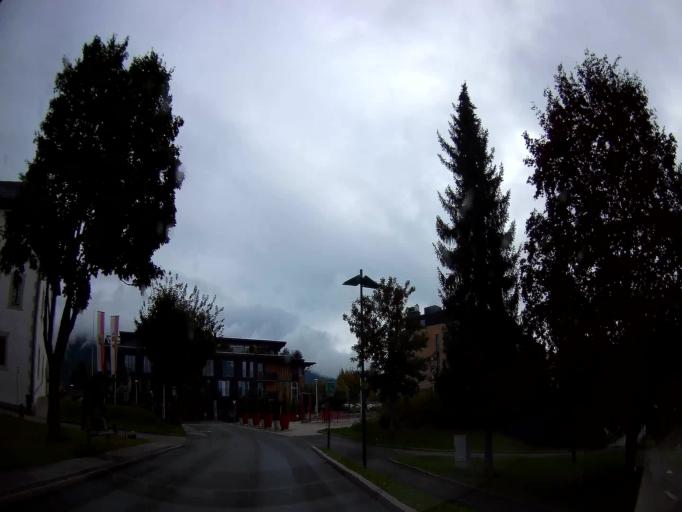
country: AT
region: Salzburg
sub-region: Politischer Bezirk Zell am See
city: Saalfelden am Steinernen Meer
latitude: 47.4208
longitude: 12.8462
